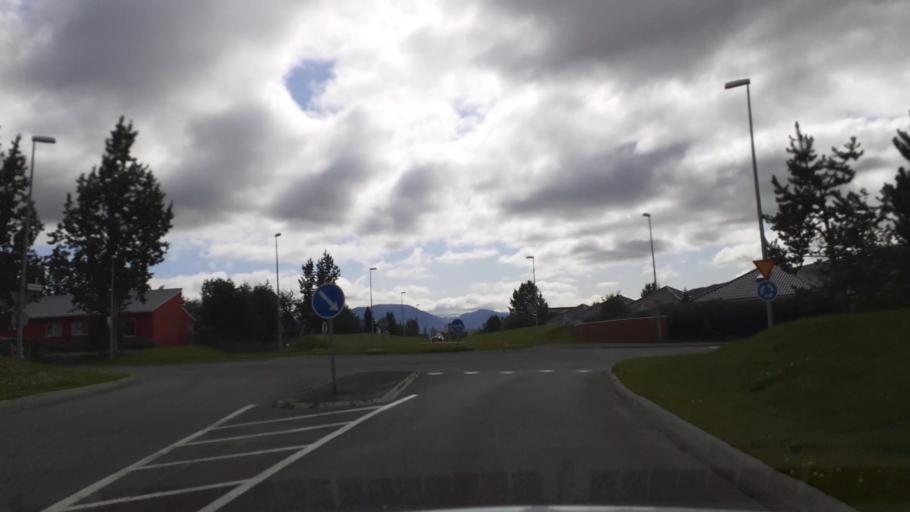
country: IS
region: Northeast
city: Akureyri
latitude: 65.6744
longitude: -18.1096
